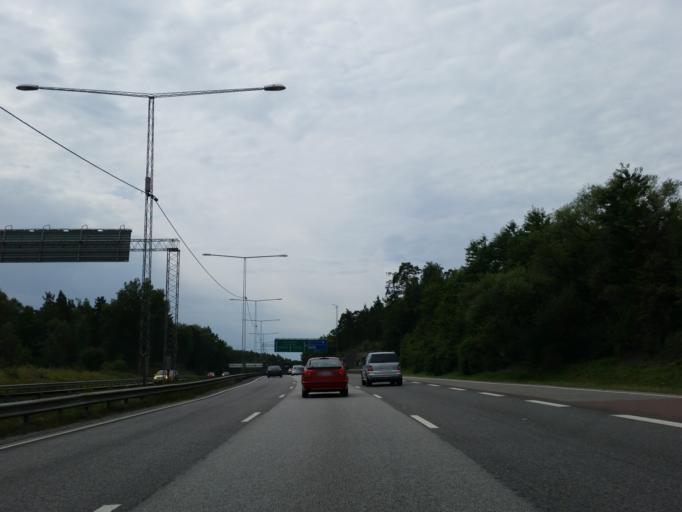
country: SE
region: Stockholm
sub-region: Botkyrka Kommun
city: Fittja
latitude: 59.2614
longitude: 17.8911
